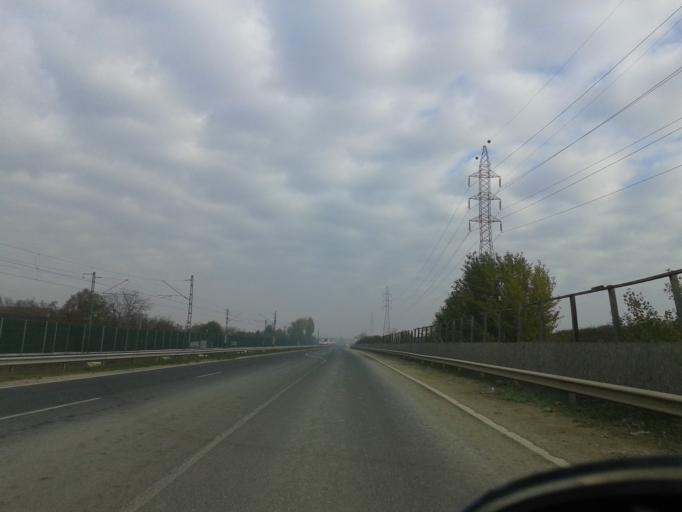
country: HU
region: Pest
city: Halasztelek
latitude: 47.3923
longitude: 18.9942
